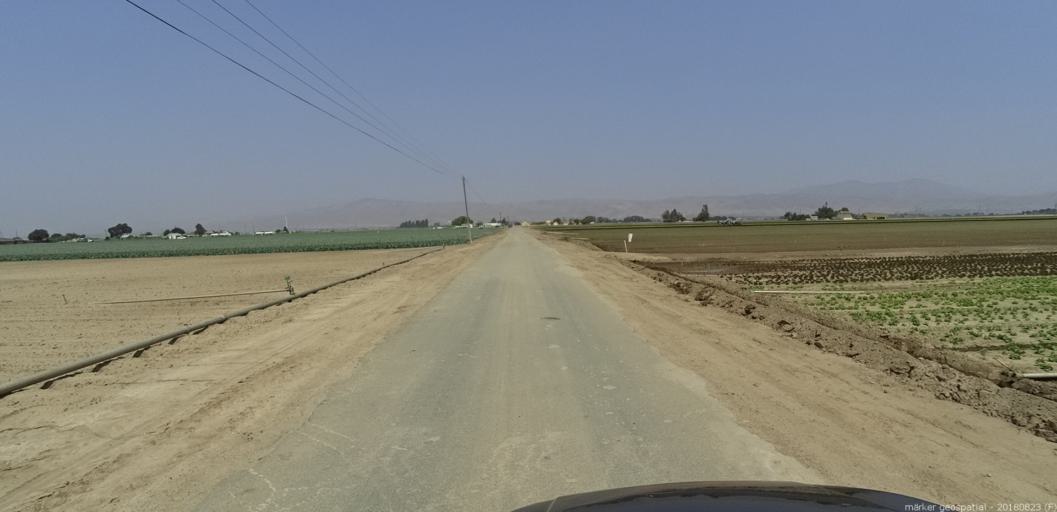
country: US
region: California
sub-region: Monterey County
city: Soledad
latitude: 36.3963
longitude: -121.3439
